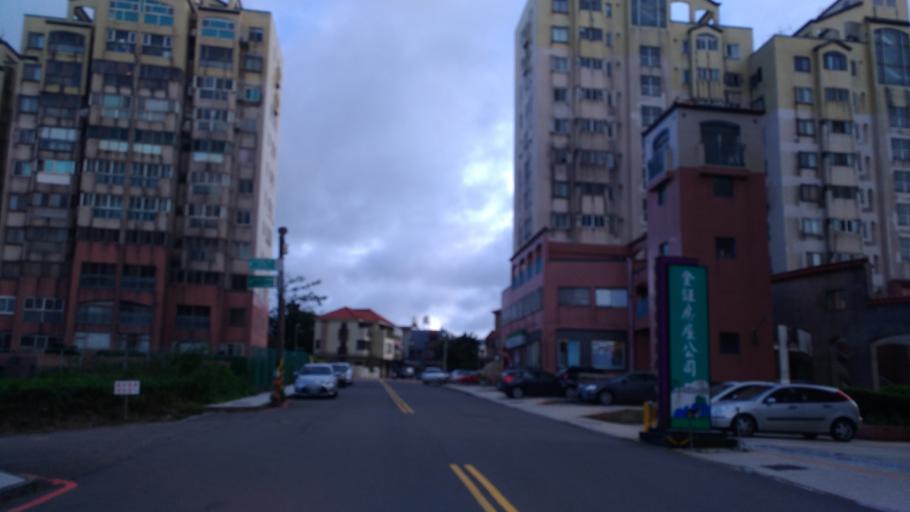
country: TW
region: Taiwan
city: Daxi
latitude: 24.8859
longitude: 121.1710
